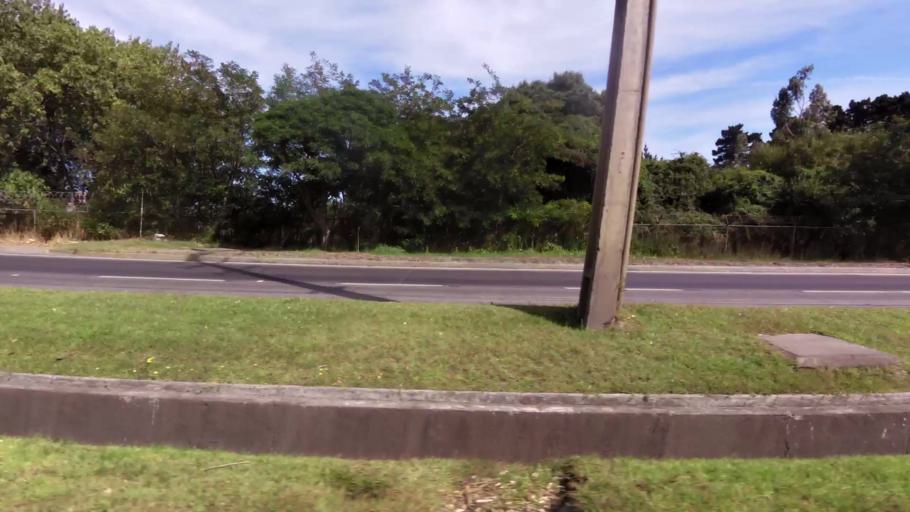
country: CL
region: Biobio
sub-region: Provincia de Concepcion
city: Talcahuano
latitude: -36.7445
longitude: -73.1215
